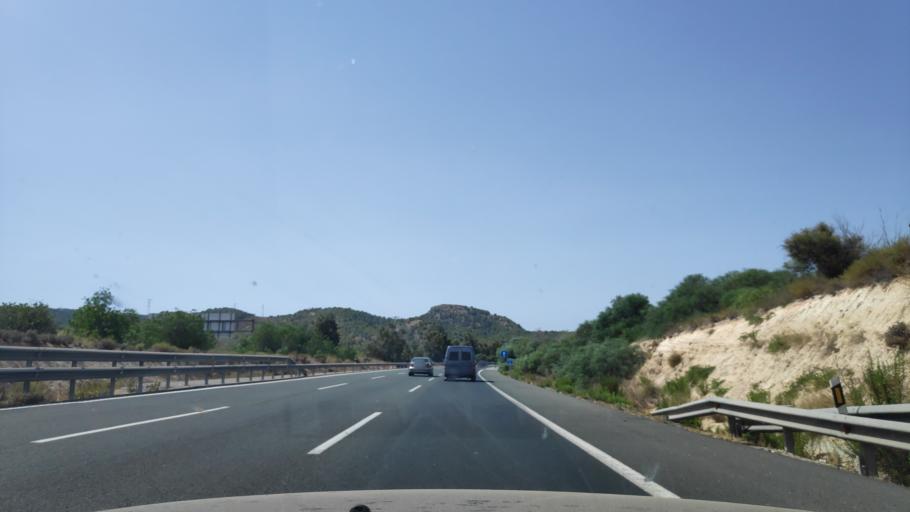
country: ES
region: Murcia
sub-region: Murcia
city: Murcia
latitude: 37.8860
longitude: -1.1385
